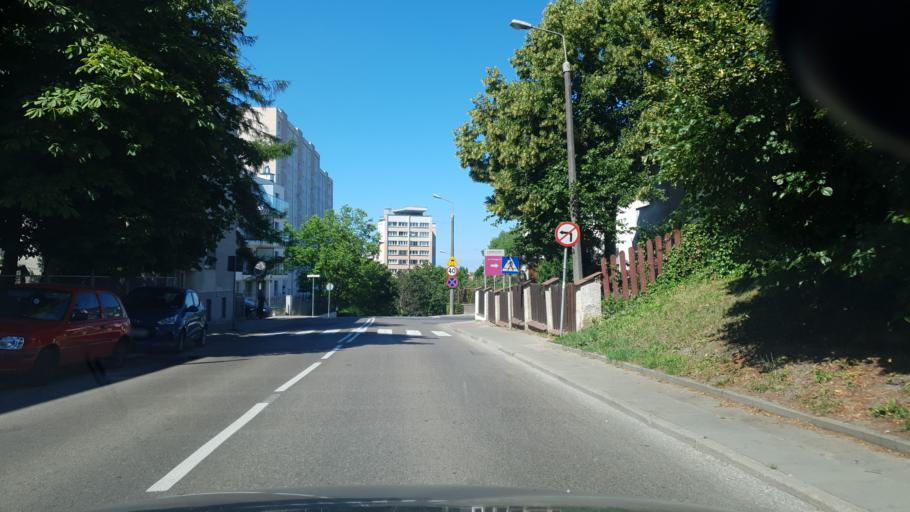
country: PL
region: Pomeranian Voivodeship
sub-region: Gdynia
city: Gdynia
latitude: 54.5047
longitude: 18.5430
